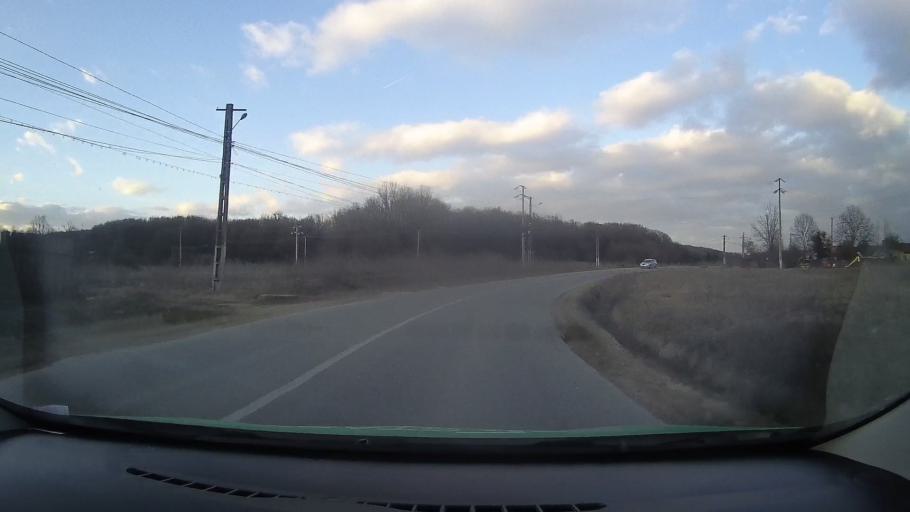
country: RO
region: Dambovita
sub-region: Comuna Gura Ocnitei
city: Gura Ocnitei
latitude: 44.9414
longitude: 25.5813
